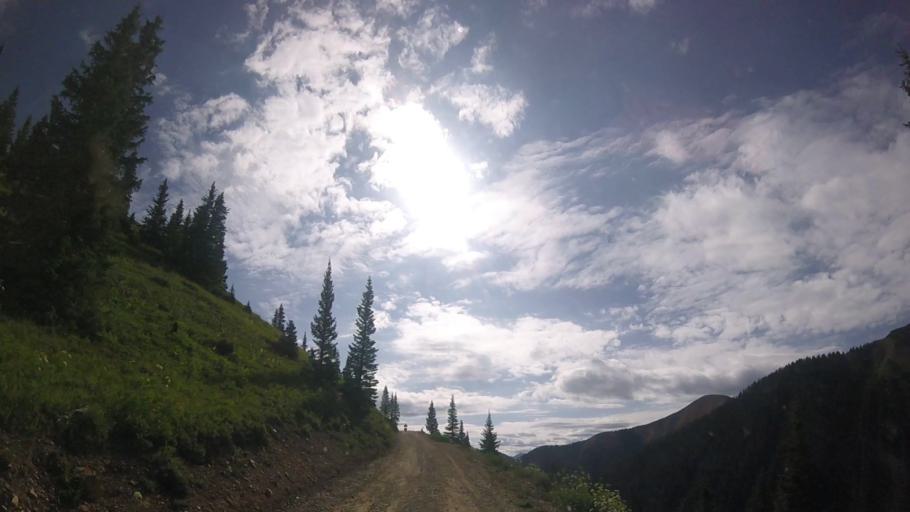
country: US
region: Colorado
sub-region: San Miguel County
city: Telluride
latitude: 37.8469
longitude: -107.7672
